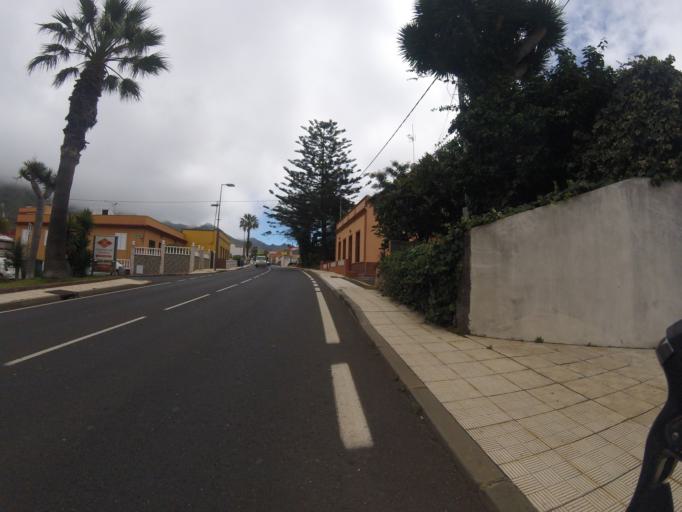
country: ES
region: Canary Islands
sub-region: Provincia de Santa Cruz de Tenerife
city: Tegueste
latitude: 28.5226
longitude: -16.3444
